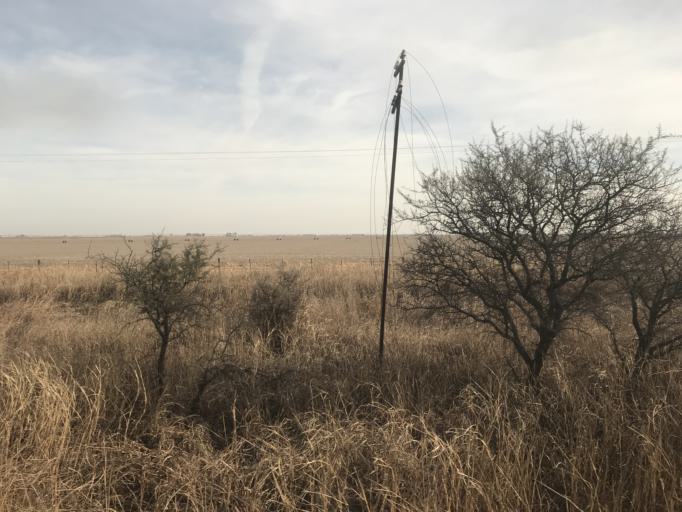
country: AR
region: Cordoba
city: Pilar
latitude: -31.7249
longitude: -63.8484
